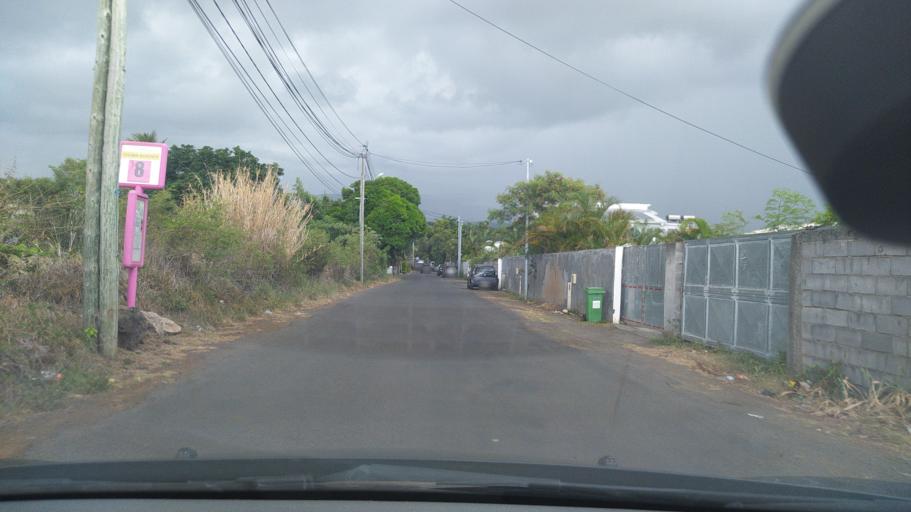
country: RE
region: Reunion
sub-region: Reunion
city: Saint-Pierre
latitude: -21.3057
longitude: 55.4643
